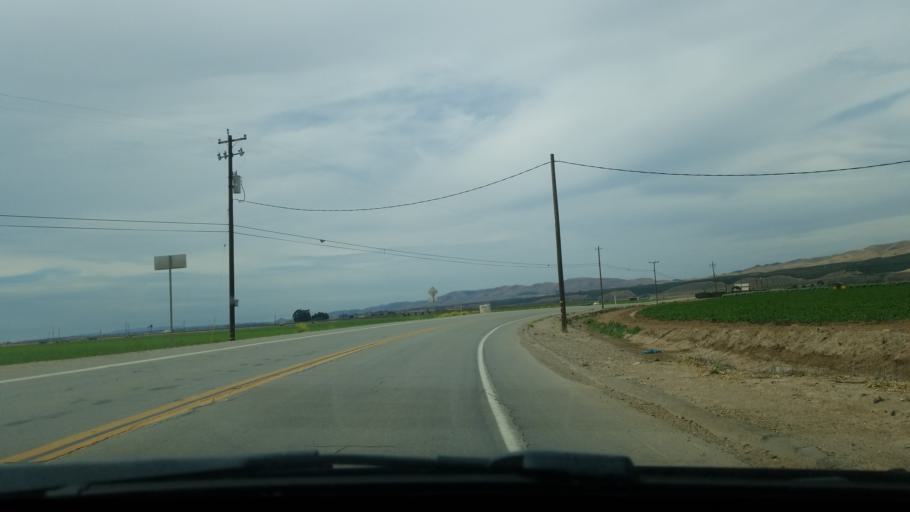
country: US
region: California
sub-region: Santa Barbara County
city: Santa Maria
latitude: 34.9106
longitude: -120.3473
